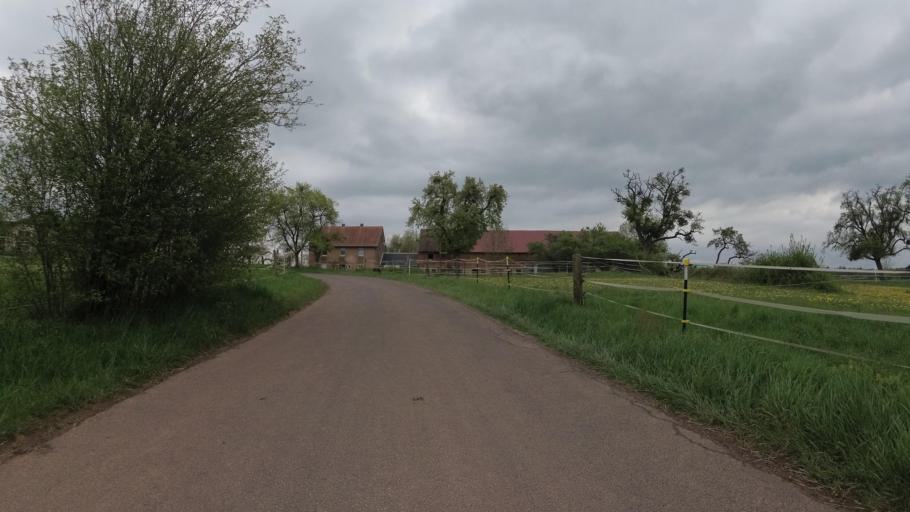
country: DE
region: Saarland
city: Merzig
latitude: 49.4099
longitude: 6.5509
